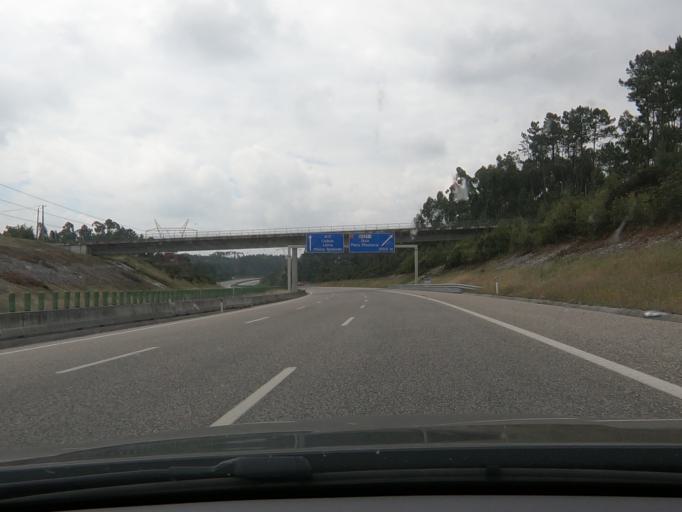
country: PT
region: Leiria
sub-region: Pombal
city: Lourical
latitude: 39.9570
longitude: -8.7746
